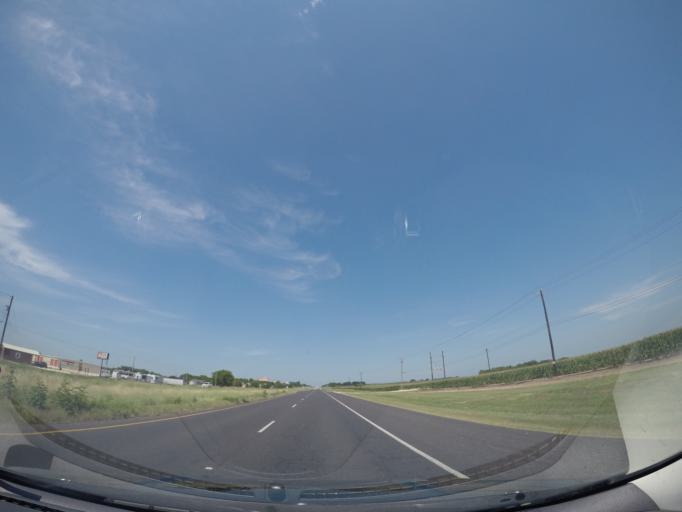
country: US
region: Texas
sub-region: Medina County
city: La Coste
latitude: 29.3646
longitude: -98.8077
